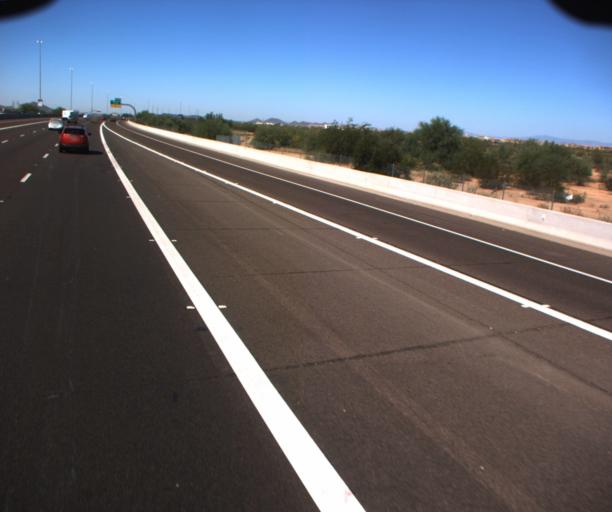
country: US
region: Arizona
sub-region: Maricopa County
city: Paradise Valley
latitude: 33.6628
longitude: -111.9469
